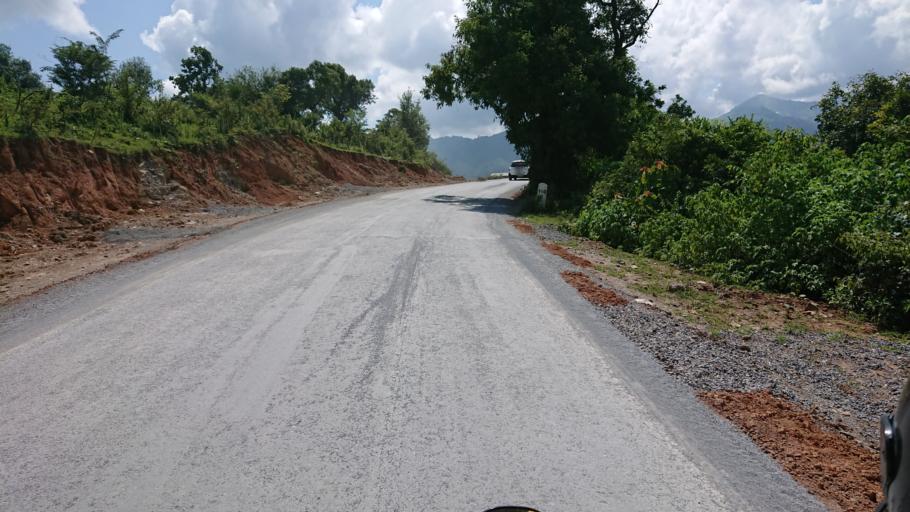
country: MM
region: Shan
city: Taunggyi
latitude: 20.8124
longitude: 97.3219
